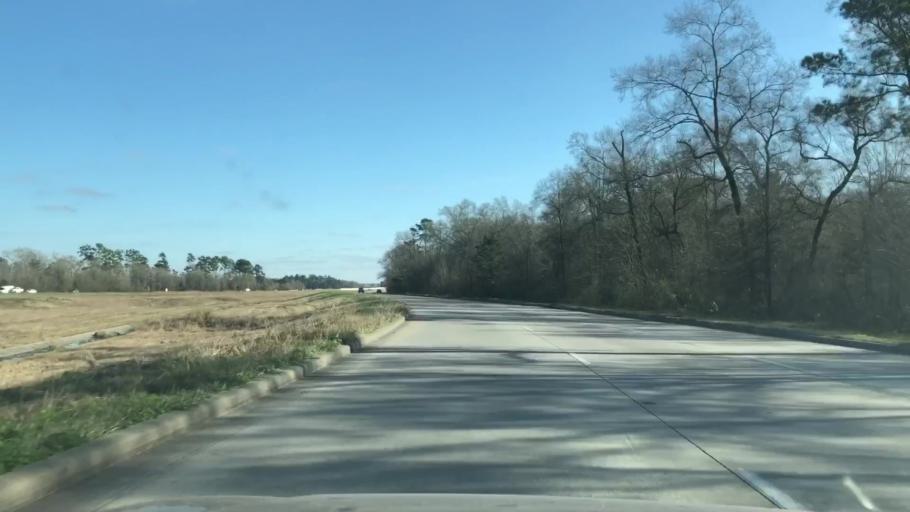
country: US
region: Texas
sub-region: Harris County
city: Cloverleaf
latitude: 29.8236
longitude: -95.1940
